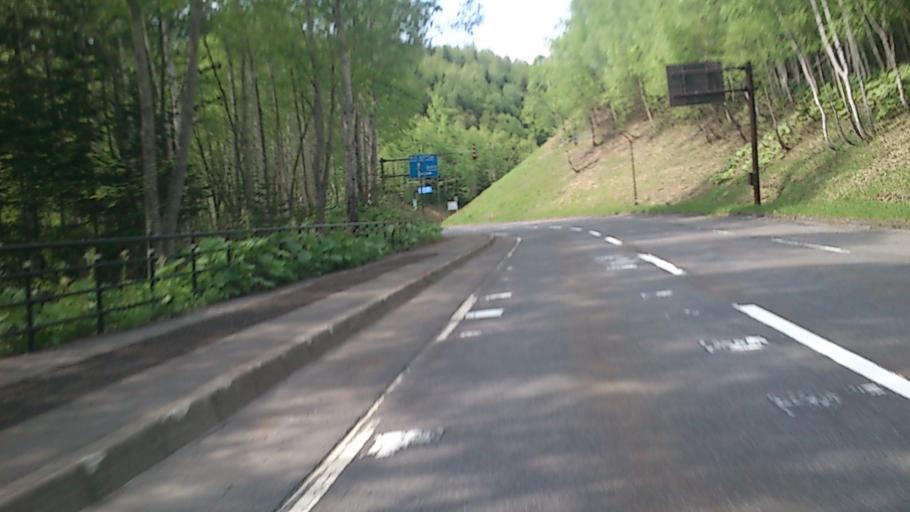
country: JP
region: Hokkaido
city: Kamikawa
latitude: 43.6636
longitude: 143.0352
